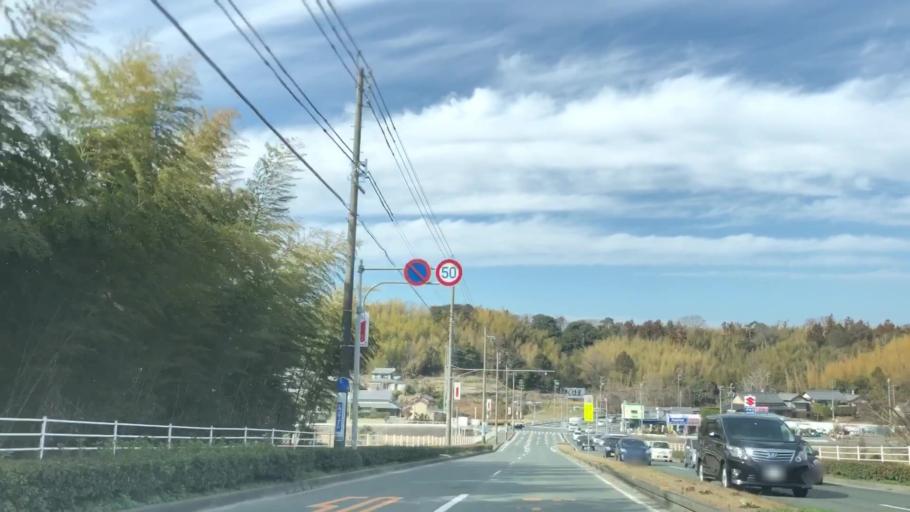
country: JP
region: Shizuoka
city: Hamamatsu
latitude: 34.7439
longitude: 137.6662
